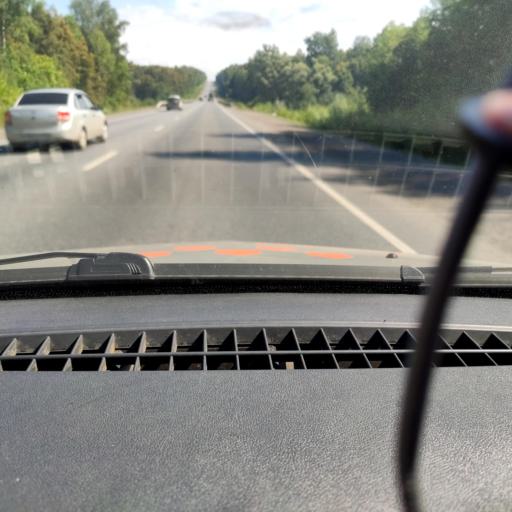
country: RU
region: Bashkortostan
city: Iglino
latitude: 54.7665
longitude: 56.4286
